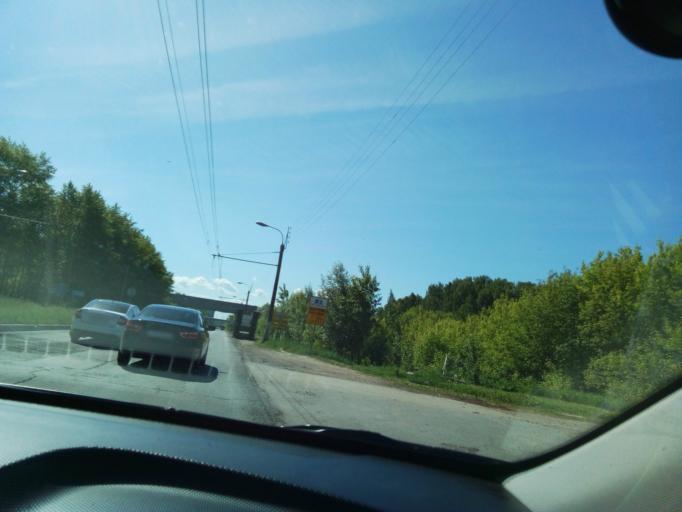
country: RU
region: Chuvashia
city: Novocheboksarsk
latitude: 56.0845
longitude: 47.5032
